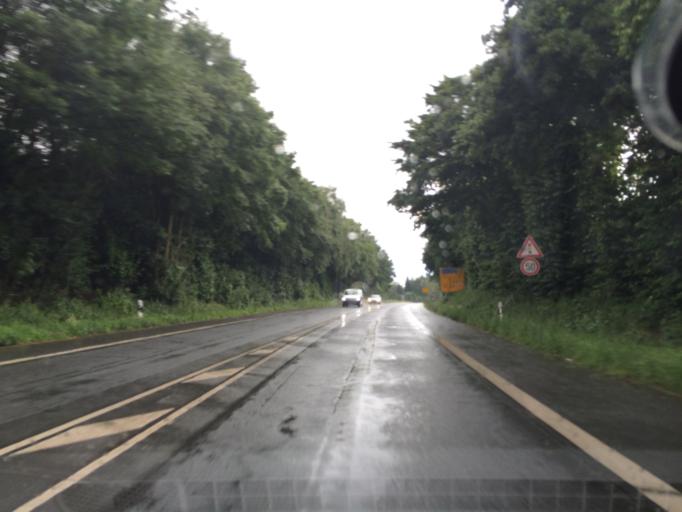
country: DE
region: North Rhine-Westphalia
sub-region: Regierungsbezirk Munster
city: Haltern
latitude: 51.7792
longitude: 7.2128
